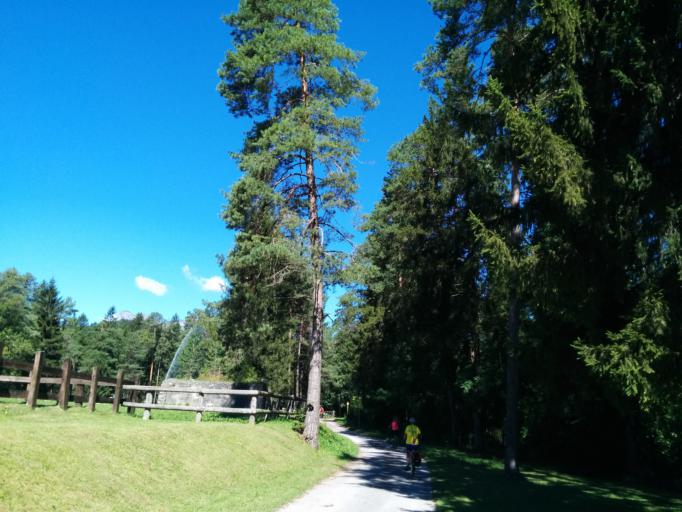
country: IT
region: Friuli Venezia Giulia
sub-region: Provincia di Udine
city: Villa Santina
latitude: 46.4086
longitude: 12.9149
